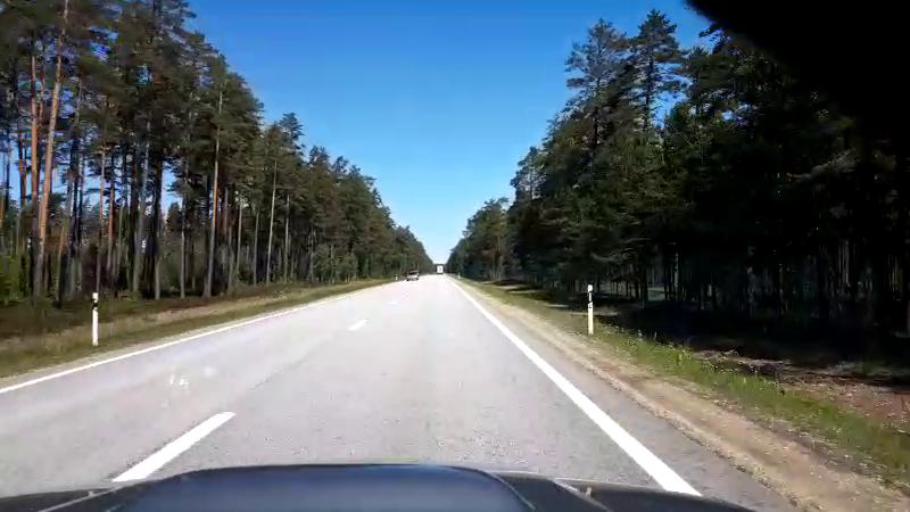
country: LV
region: Salacgrivas
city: Salacgriva
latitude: 57.5595
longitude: 24.4337
